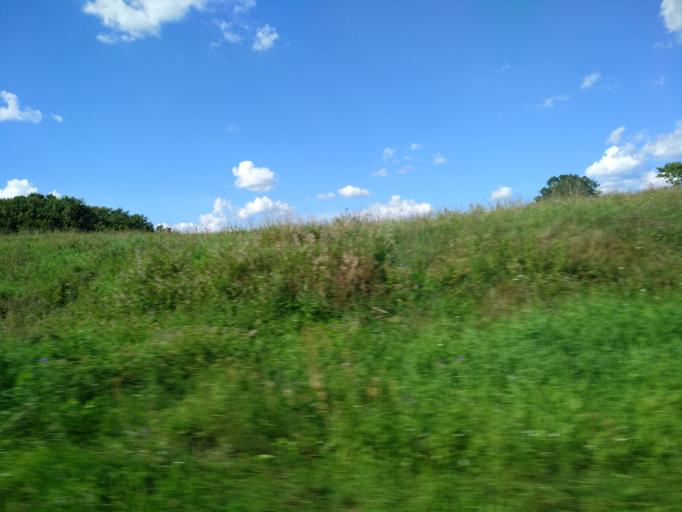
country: BY
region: Vitebsk
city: Mosar
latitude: 55.0743
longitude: 27.2278
